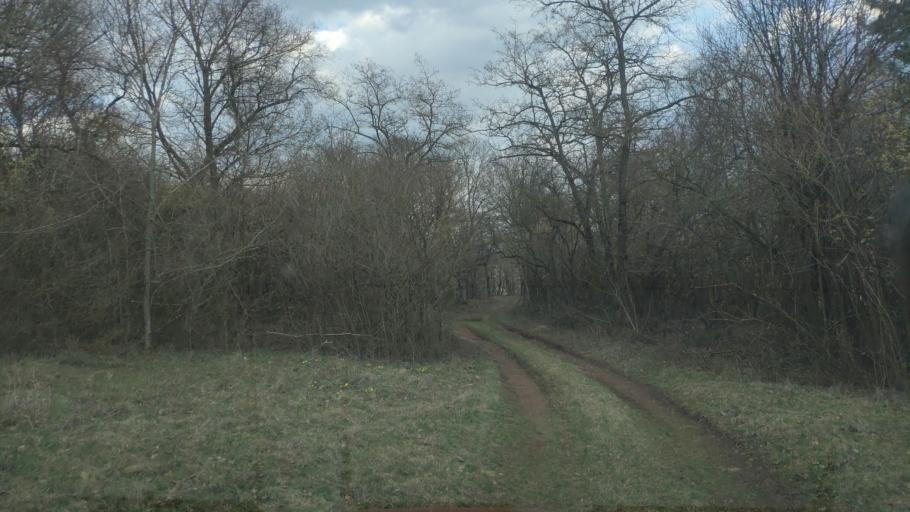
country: SK
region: Kosicky
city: Moldava nad Bodvou
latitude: 48.6203
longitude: 20.9233
